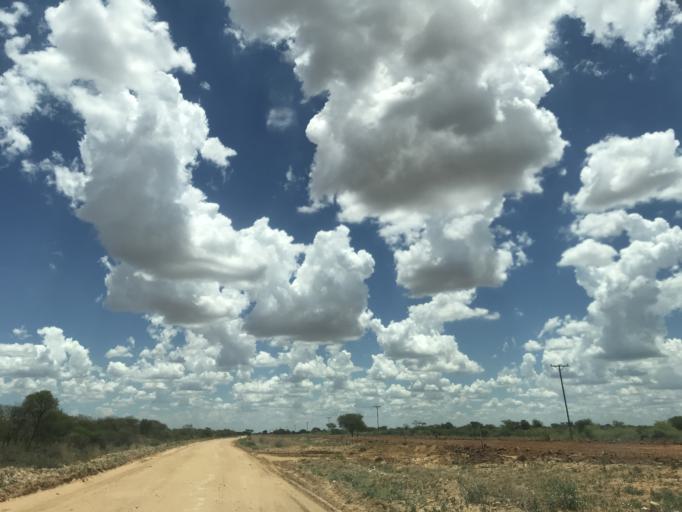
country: BW
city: Mabuli
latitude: -25.7916
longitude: 24.6551
